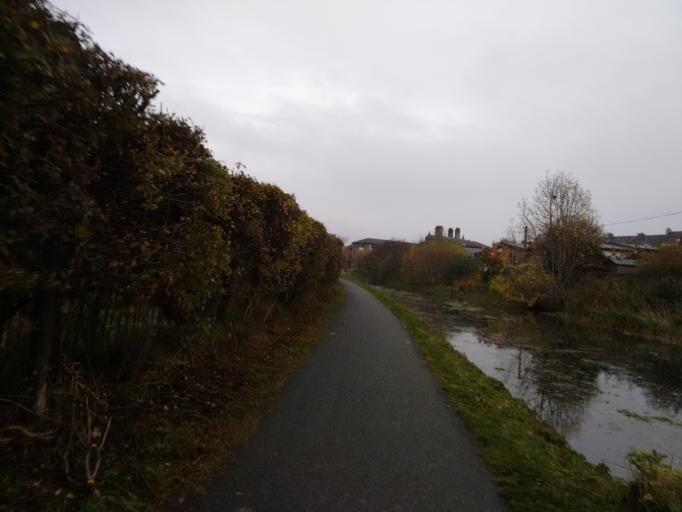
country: GB
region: Scotland
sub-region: Edinburgh
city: Colinton
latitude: 55.9253
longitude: -3.2374
